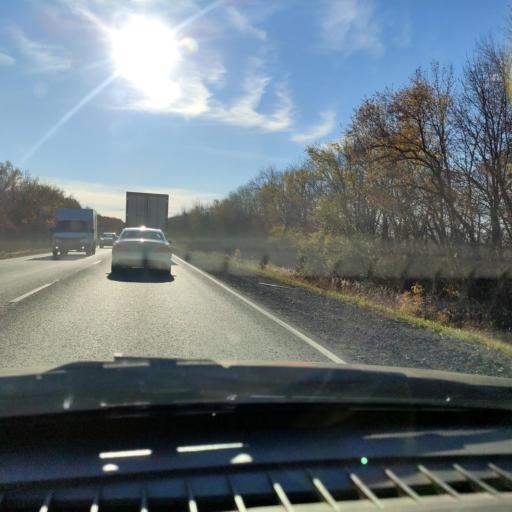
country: RU
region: Samara
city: Zhigulevsk
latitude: 53.2963
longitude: 49.3372
